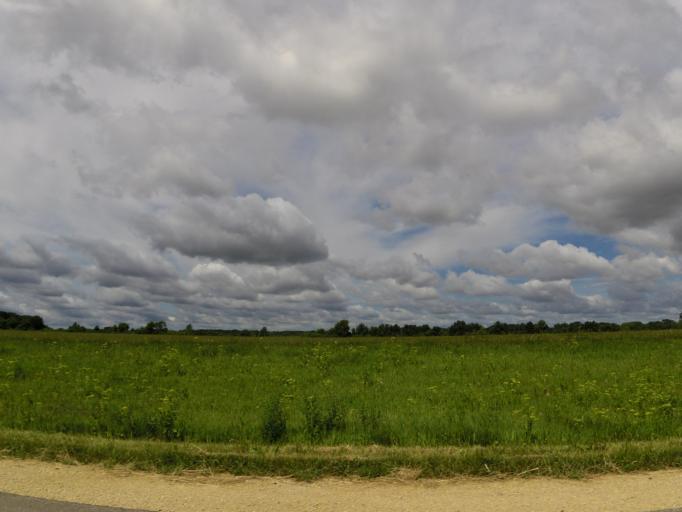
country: US
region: Minnesota
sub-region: Mower County
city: Grand Meadow
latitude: 43.7164
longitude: -92.4795
